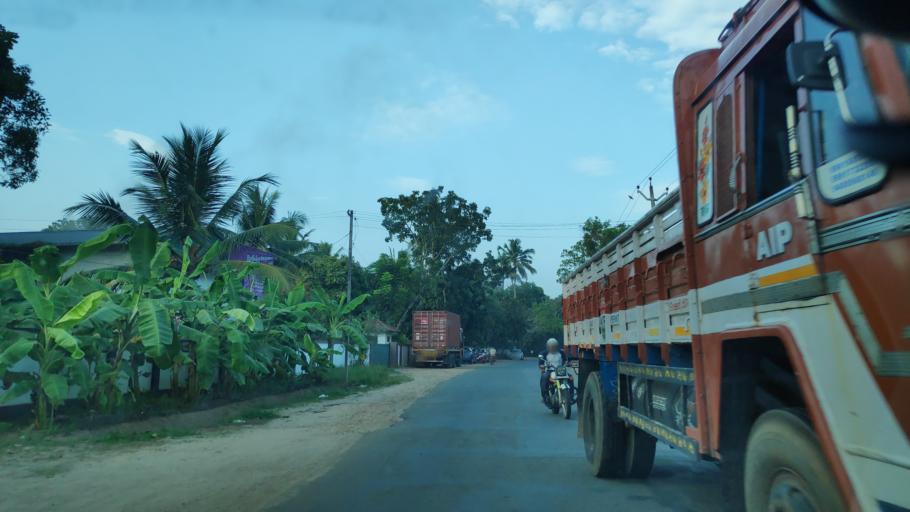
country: IN
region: Kerala
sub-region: Alappuzha
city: Shertallai
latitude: 9.6191
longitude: 76.3639
